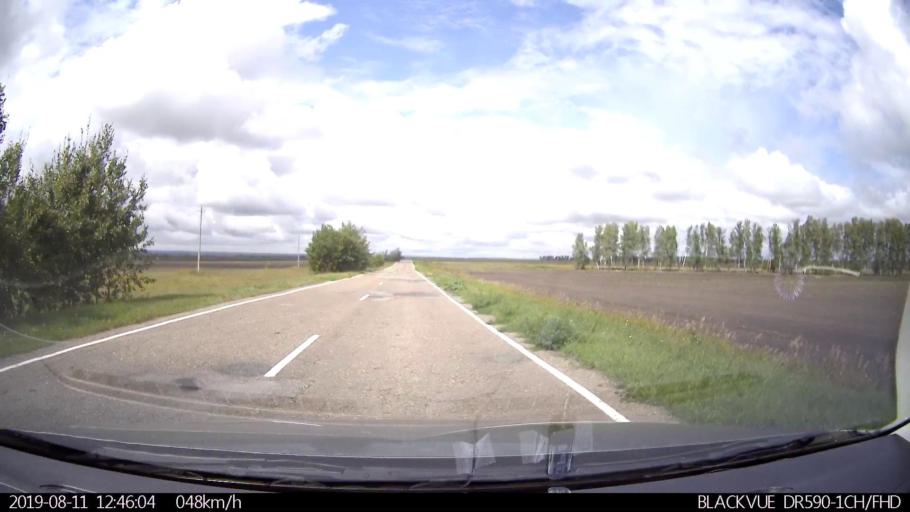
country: RU
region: Ulyanovsk
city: Ignatovka
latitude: 53.8624
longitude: 47.7224
